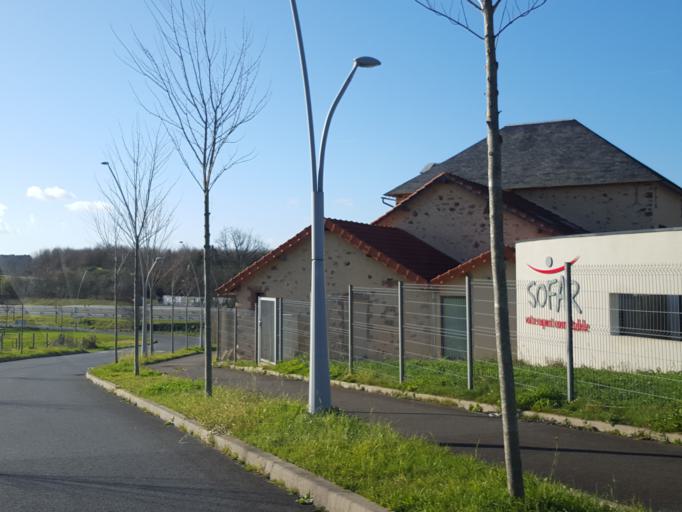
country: FR
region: Pays de la Loire
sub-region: Departement de la Vendee
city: La Roche-sur-Yon
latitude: 46.6400
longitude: -1.4361
